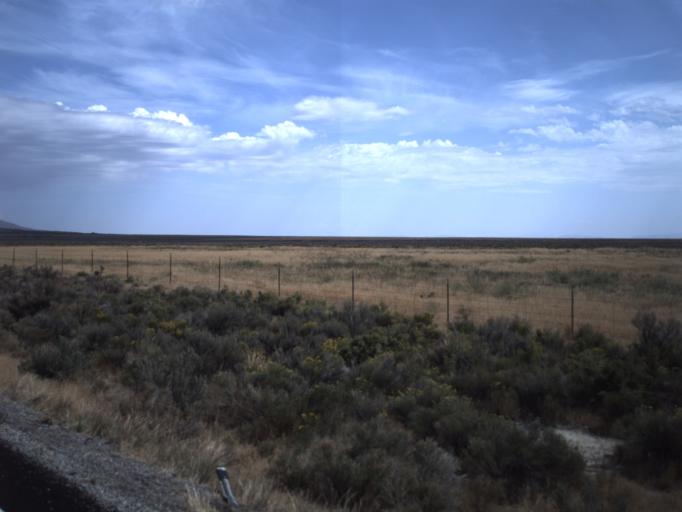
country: US
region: Idaho
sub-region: Cassia County
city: Burley
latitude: 41.7836
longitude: -113.4824
